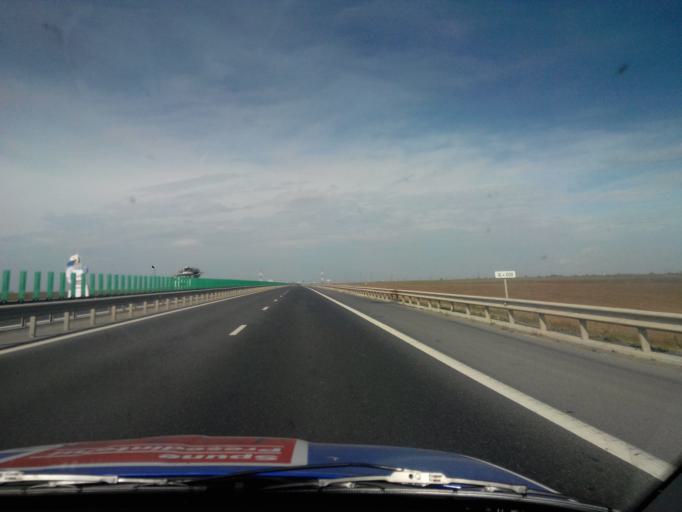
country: RO
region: Constanta
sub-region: Comuna Cumpana
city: Cumpana
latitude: 44.1241
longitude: 28.5802
